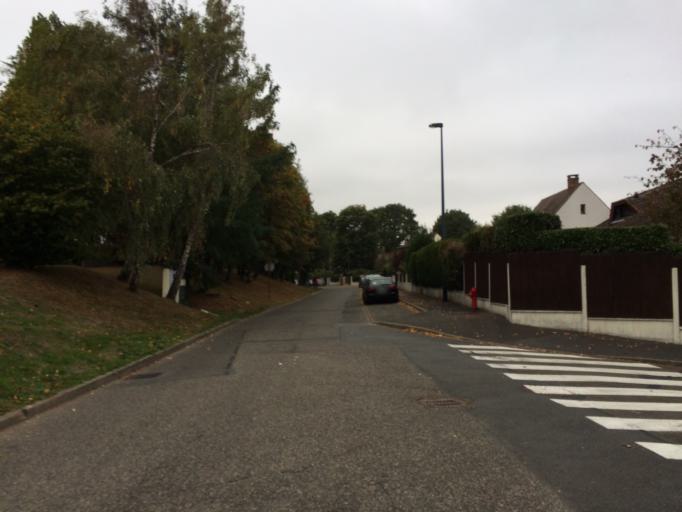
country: FR
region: Ile-de-France
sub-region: Departement de l'Essonne
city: Orsay
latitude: 48.6936
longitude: 2.2120
